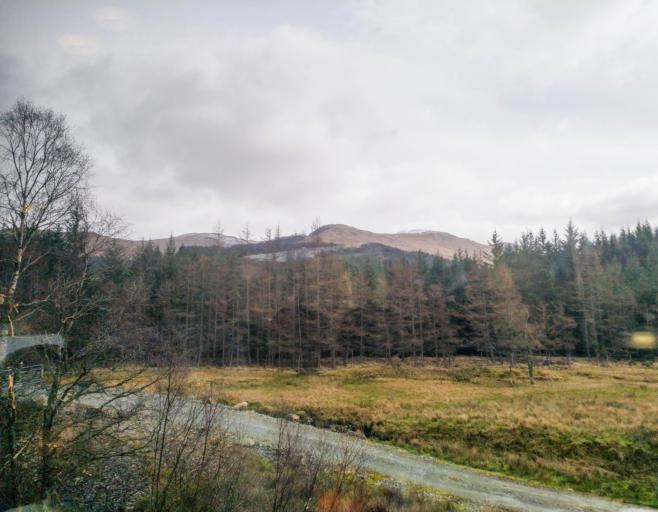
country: GB
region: Scotland
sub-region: Argyll and Bute
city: Garelochhead
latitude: 56.3788
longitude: -4.6405
